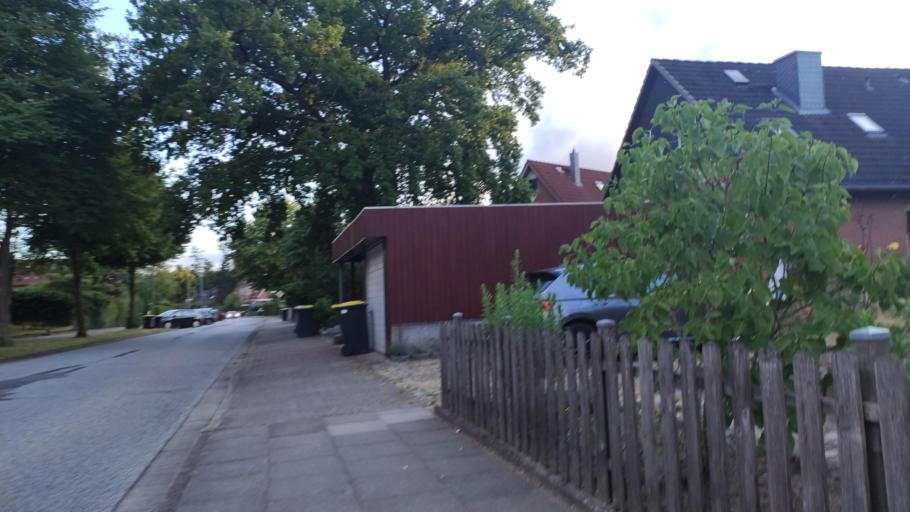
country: DE
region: Schleswig-Holstein
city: Geesthacht
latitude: 53.4393
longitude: 10.3414
